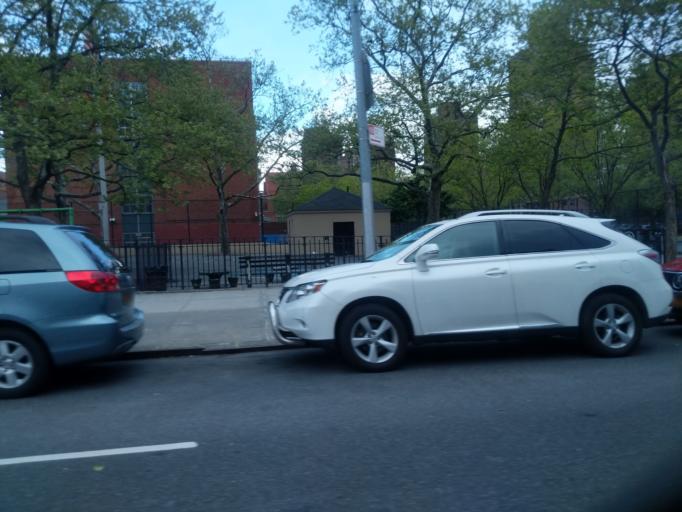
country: US
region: New York
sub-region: New York County
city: Manhattan
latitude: 40.7931
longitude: -73.9434
